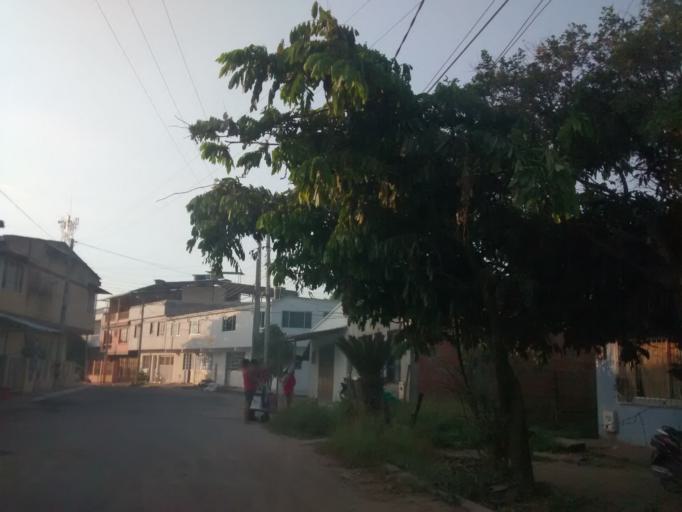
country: CO
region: Cundinamarca
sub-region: Girardot
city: Girardot City
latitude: 4.3164
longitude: -74.7824
